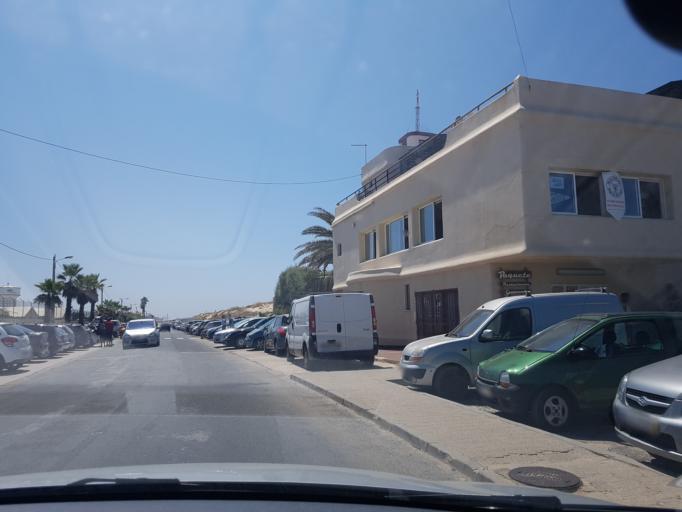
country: PT
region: Faro
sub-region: Faro
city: Faro
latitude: 37.0063
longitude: -7.9922
